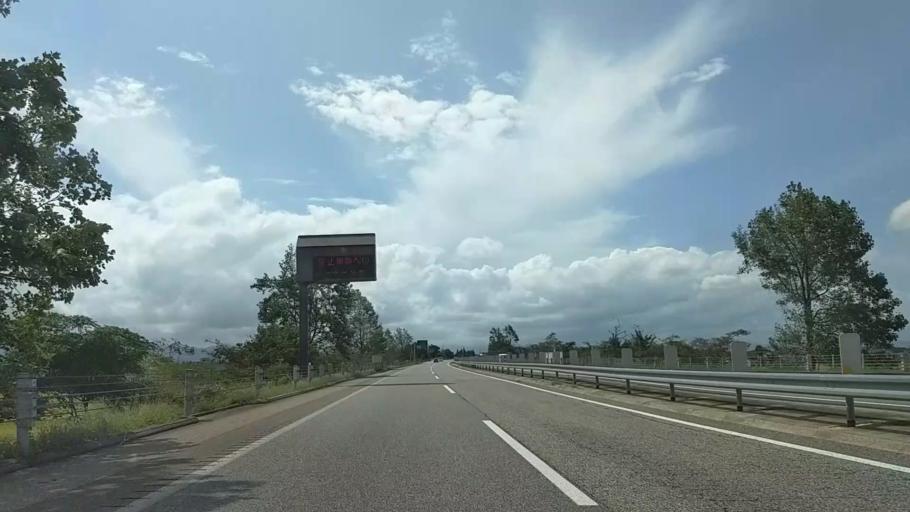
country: JP
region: Toyama
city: Kamiichi
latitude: 36.6900
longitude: 137.3288
